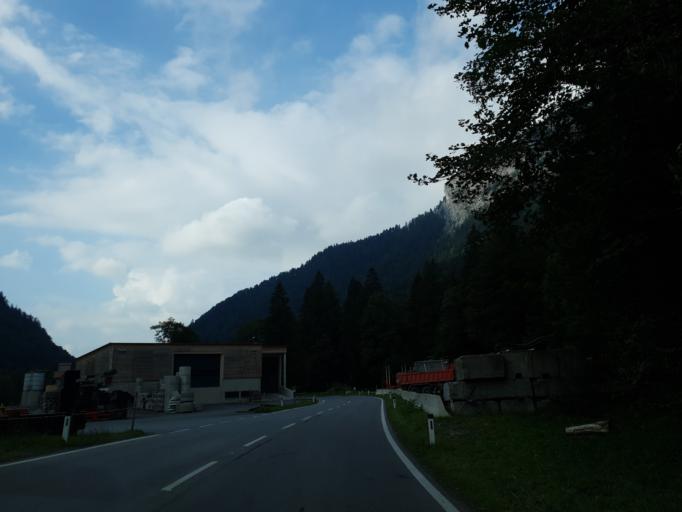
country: AT
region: Vorarlberg
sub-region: Politischer Bezirk Bregenz
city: Au
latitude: 47.3299
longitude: 9.9718
